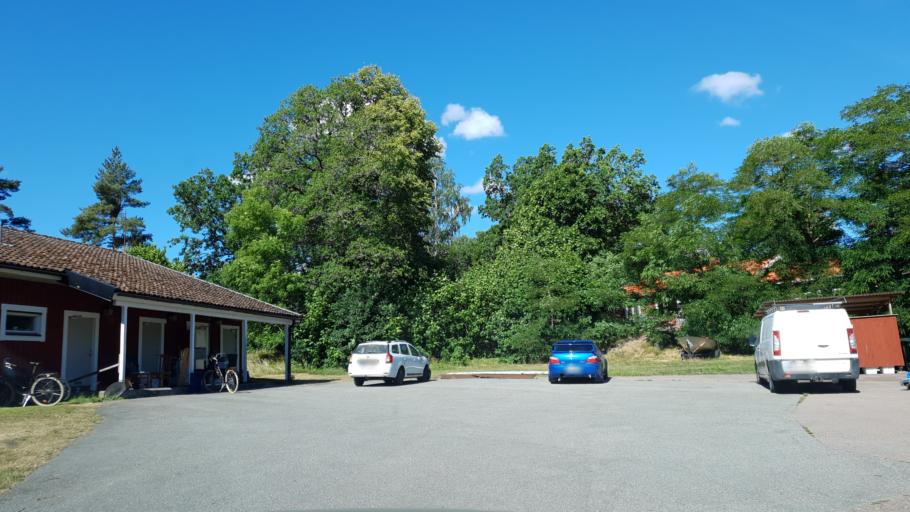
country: SE
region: Kalmar
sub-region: Emmaboda Kommun
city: Emmaboda
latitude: 56.6227
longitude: 15.6703
